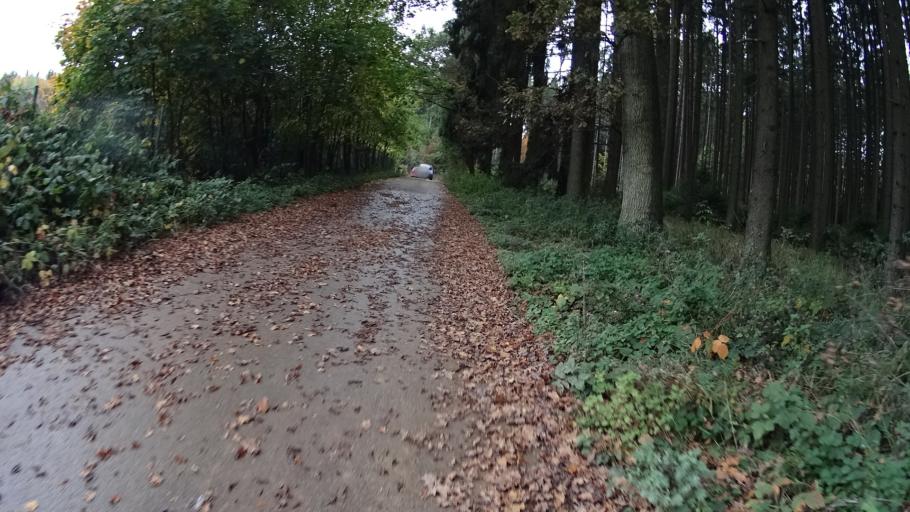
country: DE
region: Bavaria
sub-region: Upper Bavaria
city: Hitzhofen
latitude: 48.8503
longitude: 11.2991
